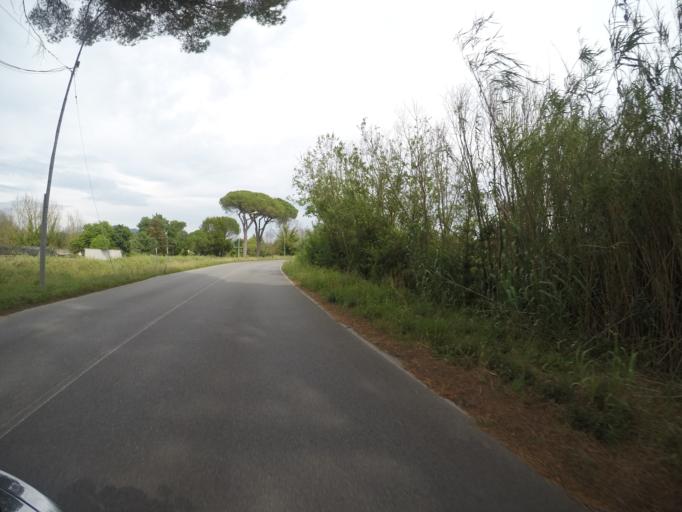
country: IT
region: Tuscany
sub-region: Province of Pisa
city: Madonna dell'Acqua
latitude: 43.7400
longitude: 10.3795
